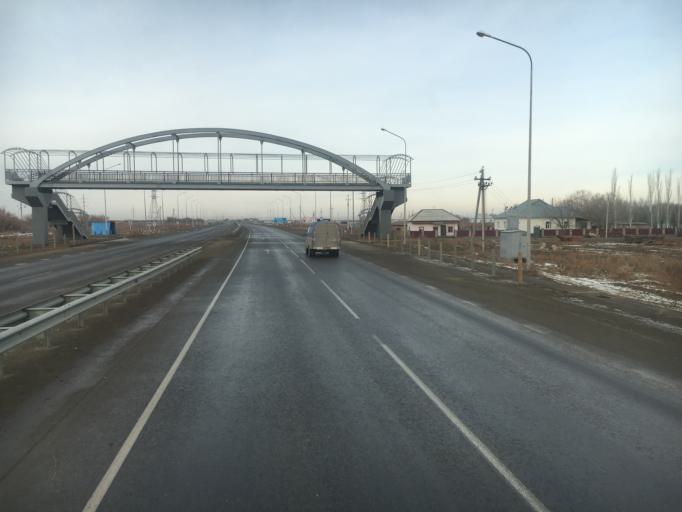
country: KZ
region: Qyzylorda
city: Shieli
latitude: 44.1377
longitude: 66.9686
